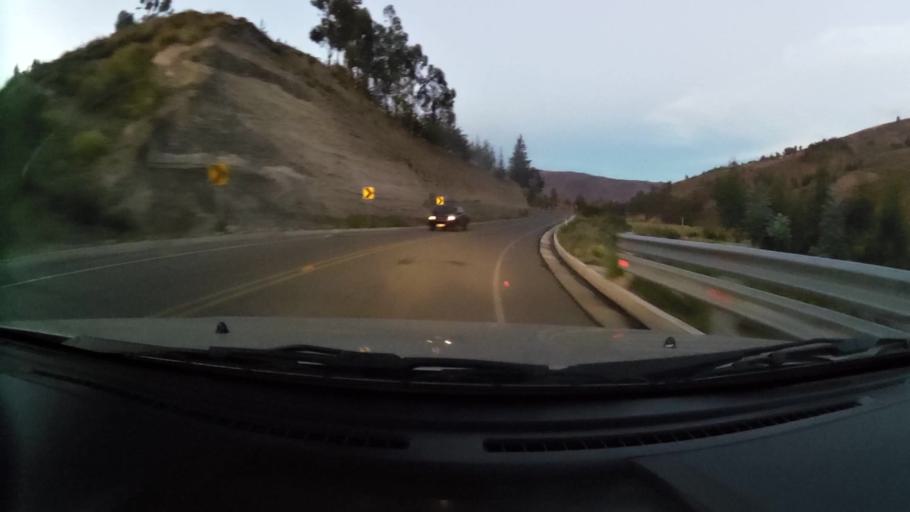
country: EC
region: Chimborazo
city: Riobamba
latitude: -1.8938
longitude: -78.6884
